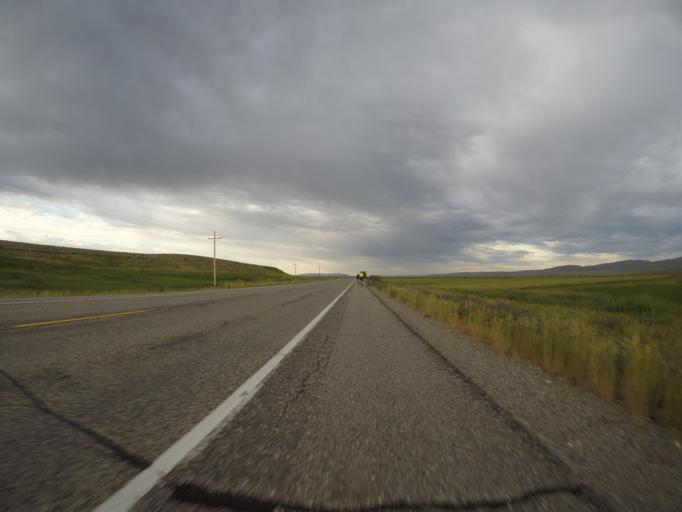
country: US
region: Utah
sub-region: Rich County
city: Randolph
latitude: 41.9737
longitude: -110.9451
